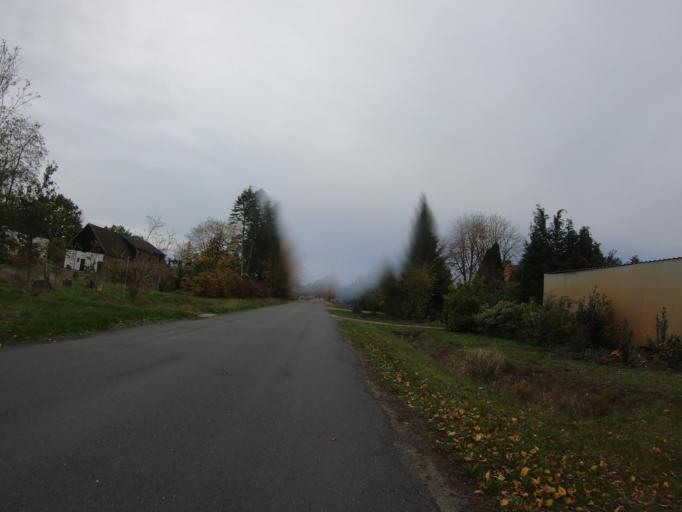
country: DE
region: Lower Saxony
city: Isenbuttel
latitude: 52.4690
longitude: 10.5974
